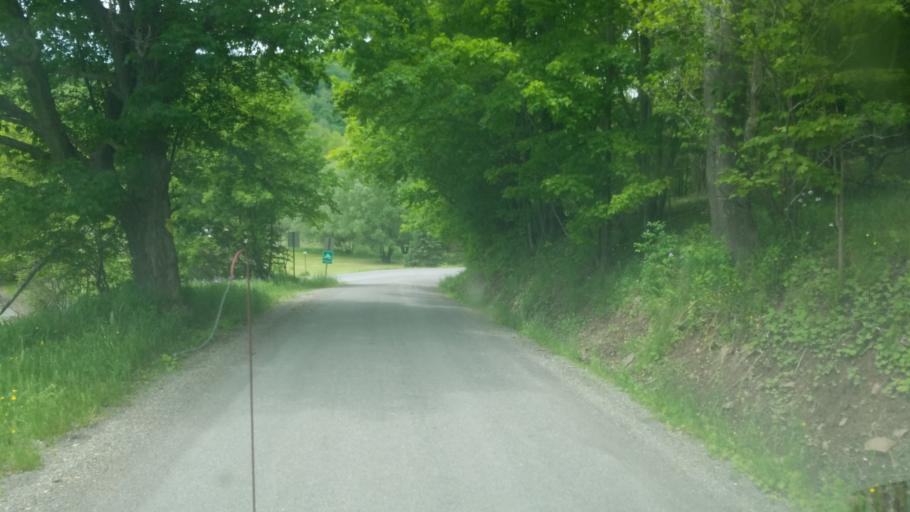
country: US
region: Pennsylvania
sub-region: Tioga County
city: Westfield
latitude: 41.8951
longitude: -77.6042
